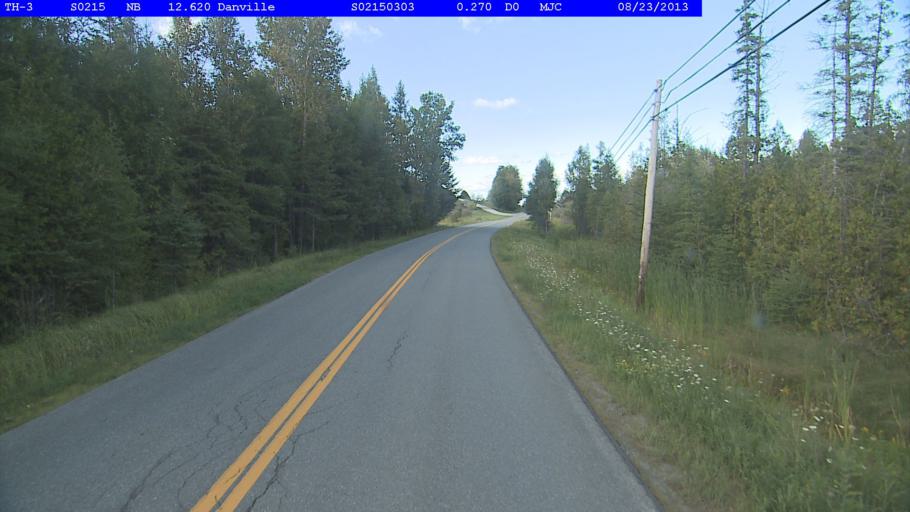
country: US
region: Vermont
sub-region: Caledonia County
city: Saint Johnsbury
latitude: 44.3698
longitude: -72.1474
